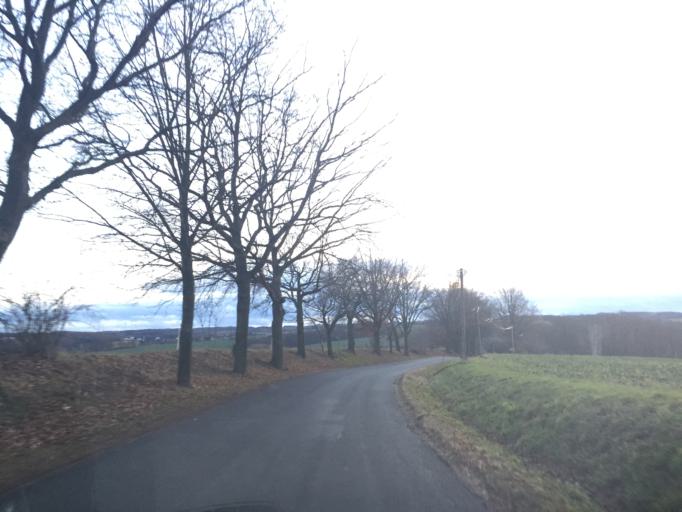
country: DE
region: Thuringia
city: Schmolln
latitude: 50.8973
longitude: 12.3319
